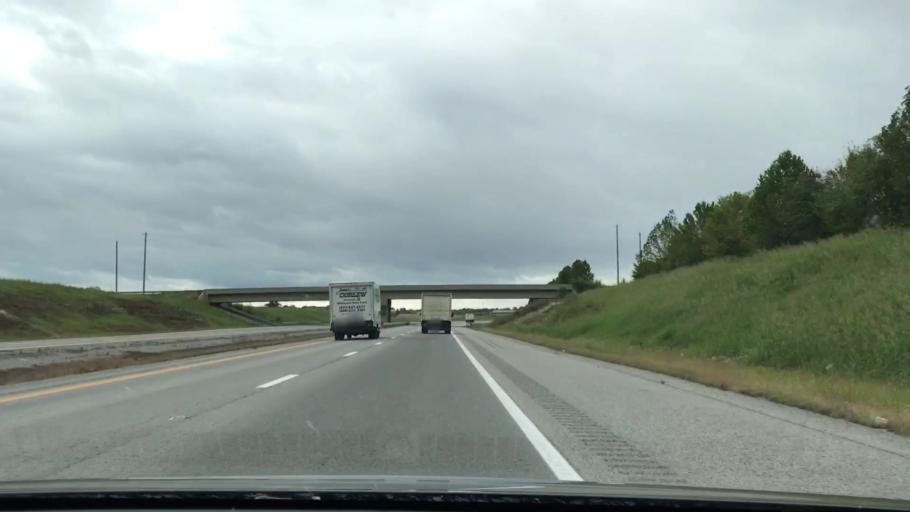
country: US
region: Kentucky
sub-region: Christian County
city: Hopkinsville
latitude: 36.7705
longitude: -87.4992
